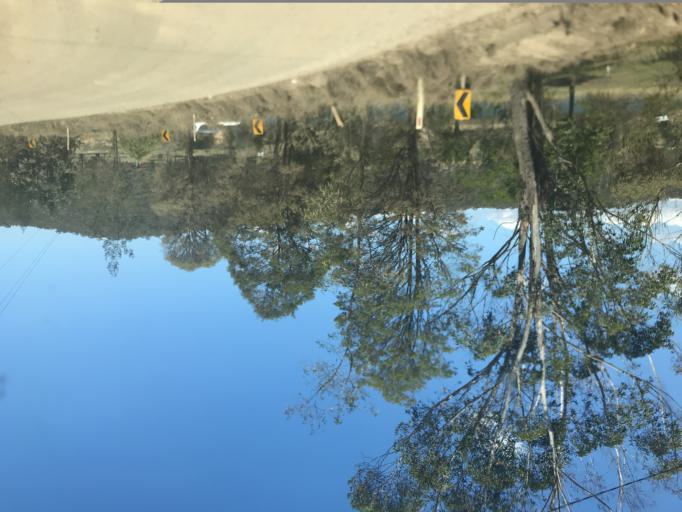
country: AU
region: New South Wales
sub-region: Hawkesbury
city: Pitt Town
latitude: -33.4355
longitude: 150.8943
